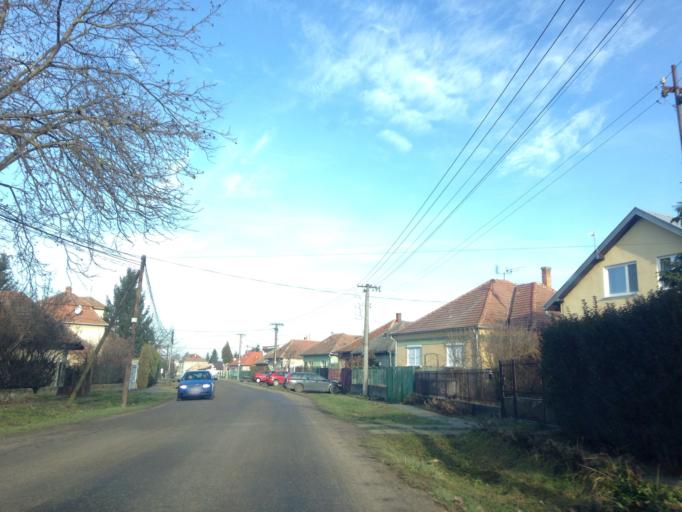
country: SK
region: Nitriansky
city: Svodin
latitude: 47.9239
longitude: 18.4034
